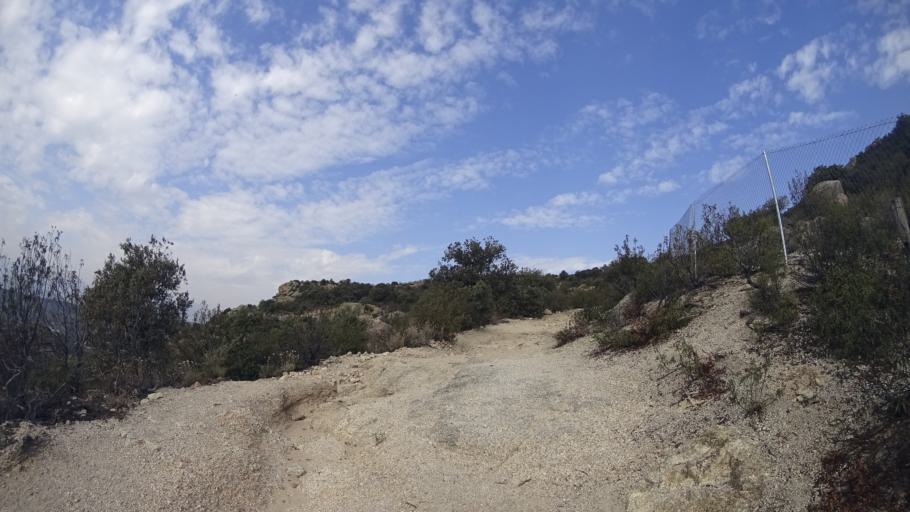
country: ES
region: Madrid
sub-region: Provincia de Madrid
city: Hoyo de Manzanares
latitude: 40.6231
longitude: -3.9296
